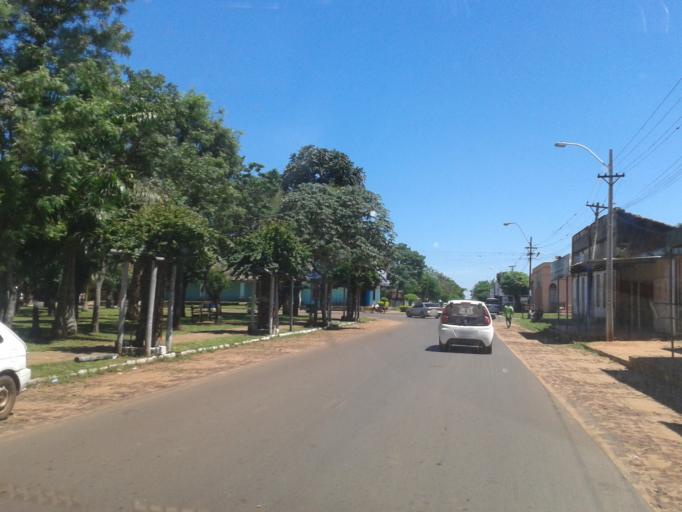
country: PY
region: Misiones
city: Santa Rosa
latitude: -26.8863
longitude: -56.8485
